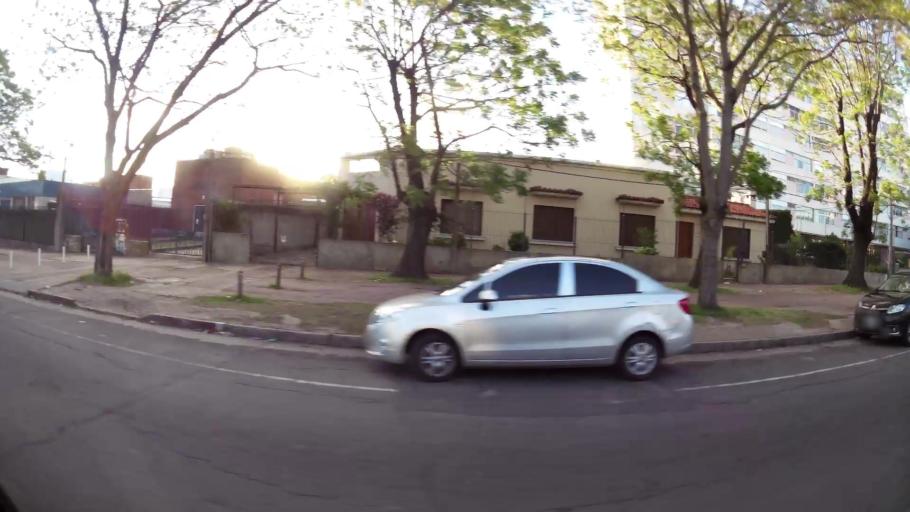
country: UY
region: Montevideo
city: Montevideo
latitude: -34.8836
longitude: -56.1526
